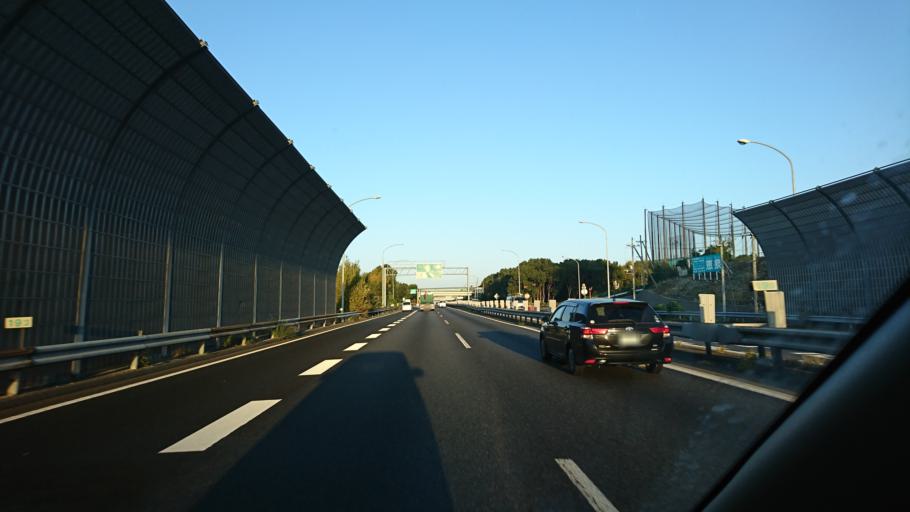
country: JP
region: Hyogo
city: Akashi
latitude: 34.7085
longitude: 134.9470
